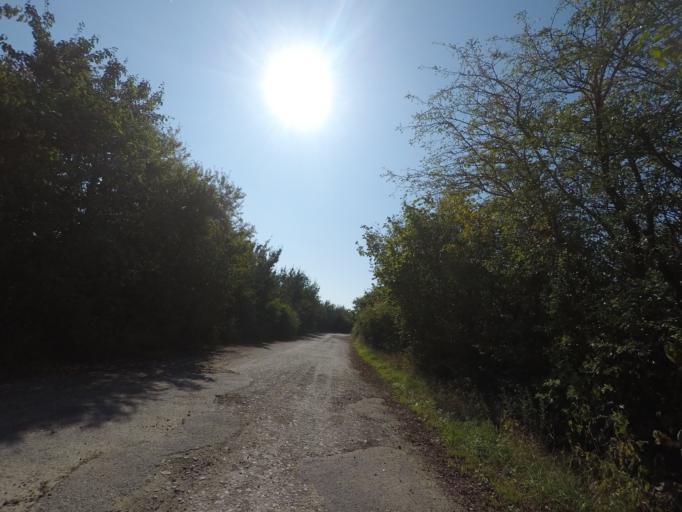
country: LU
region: Luxembourg
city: Kirchberg
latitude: 49.6130
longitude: 6.1754
